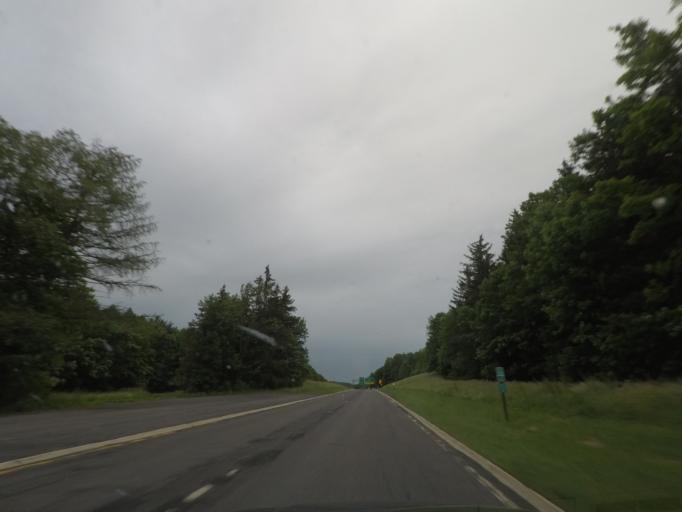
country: US
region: New York
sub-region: Columbia County
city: Chatham
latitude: 42.3829
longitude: -73.5614
